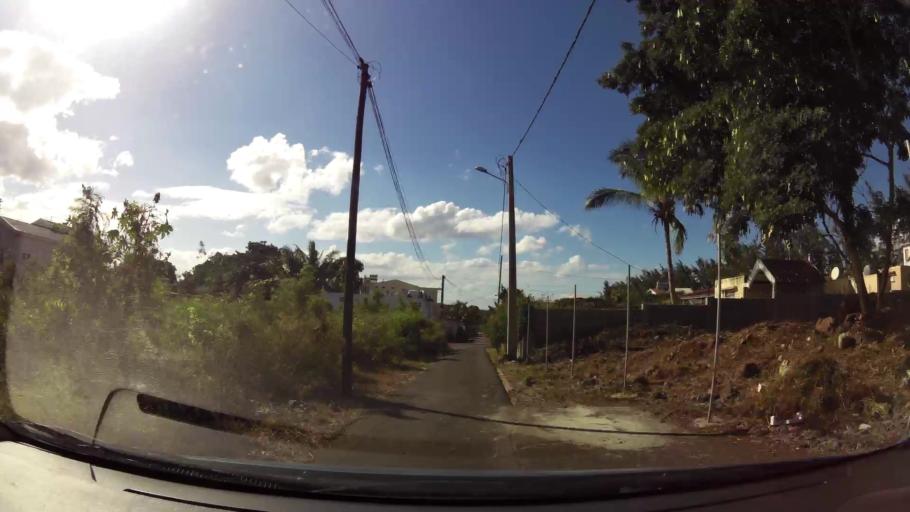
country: MU
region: Black River
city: Albion
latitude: -20.2195
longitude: 57.4047
